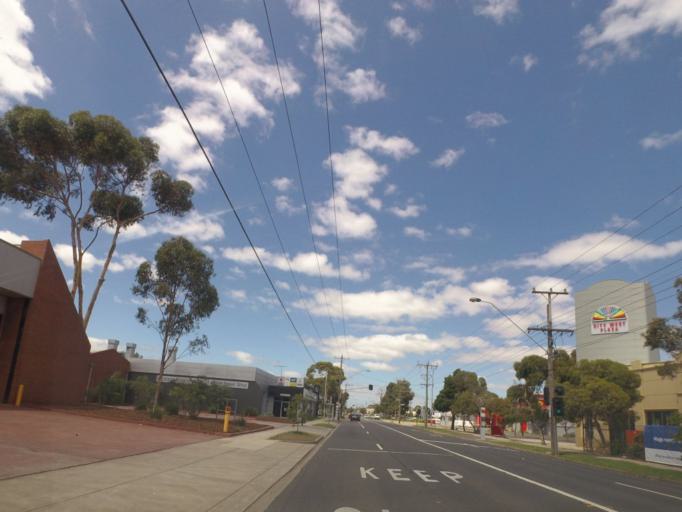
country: AU
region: Victoria
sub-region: Brimbank
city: Sunshine North
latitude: -37.7744
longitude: 144.8293
